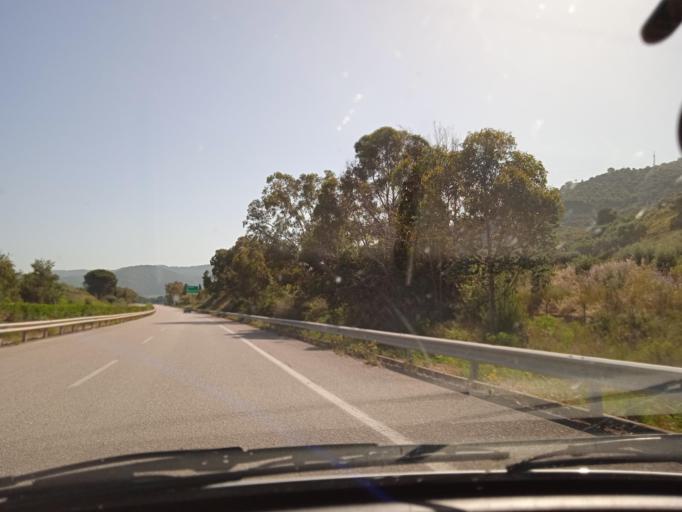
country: IT
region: Sicily
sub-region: Messina
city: Rocca di Capri Leone
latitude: 38.0946
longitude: 14.7017
